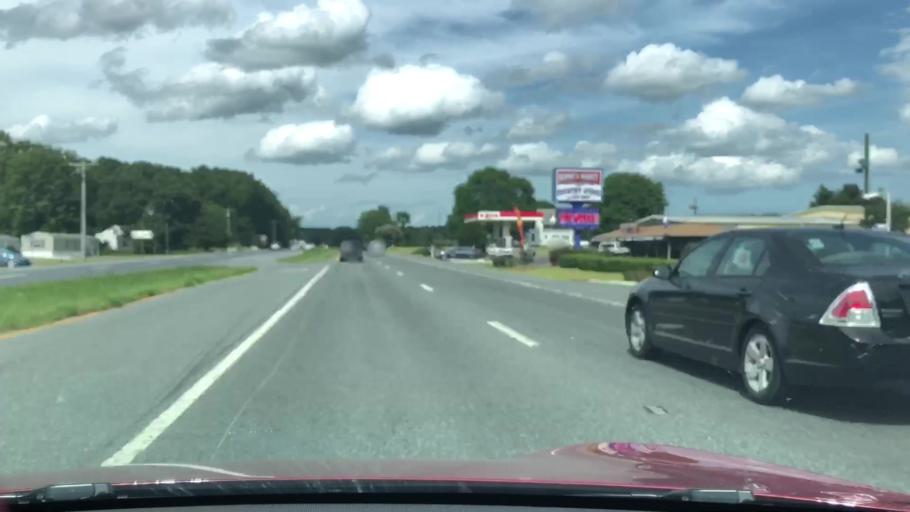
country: US
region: Virginia
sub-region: Accomack County
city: Wattsville
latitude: 37.9521
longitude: -75.5369
